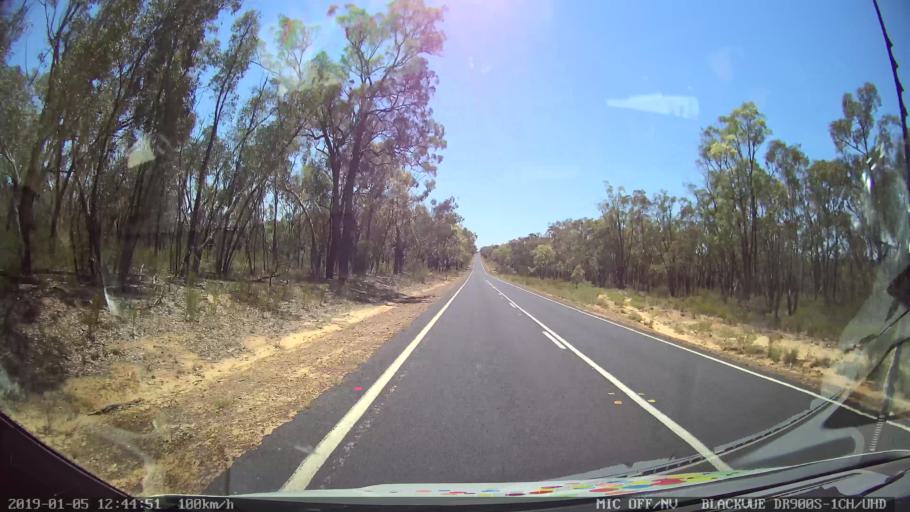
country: AU
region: New South Wales
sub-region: Warrumbungle Shire
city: Coonabarabran
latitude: -31.1337
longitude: 149.5425
